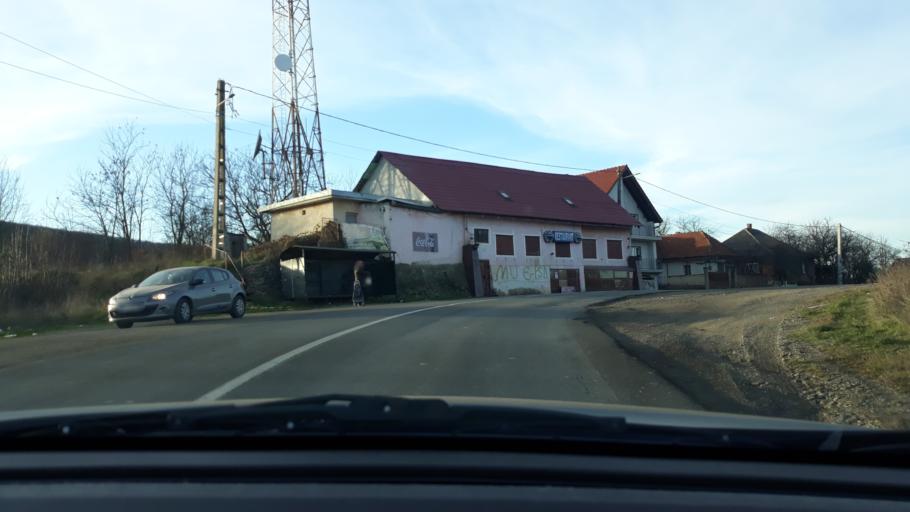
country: RO
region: Salaj
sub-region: Comuna Marca
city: Marca
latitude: 47.2268
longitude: 22.5530
